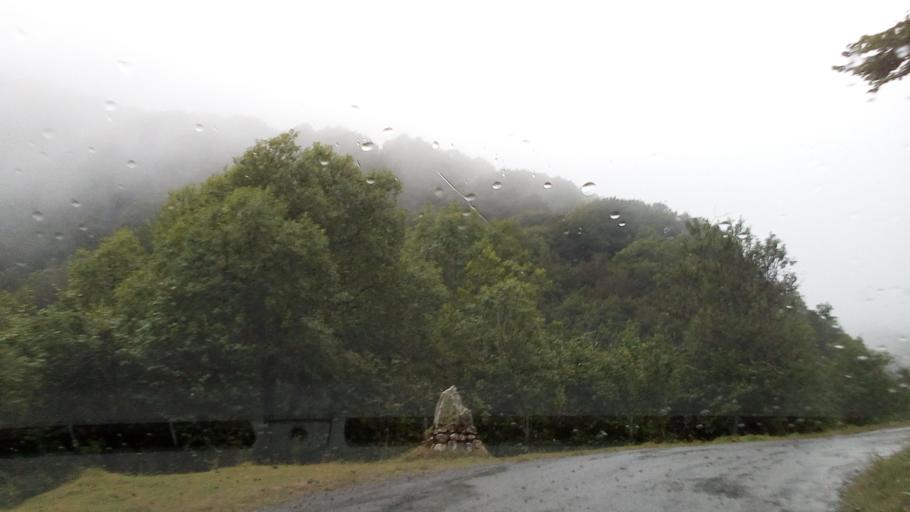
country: FR
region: Midi-Pyrenees
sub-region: Departement des Hautes-Pyrenees
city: Cauterets
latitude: 42.9198
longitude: -0.2531
